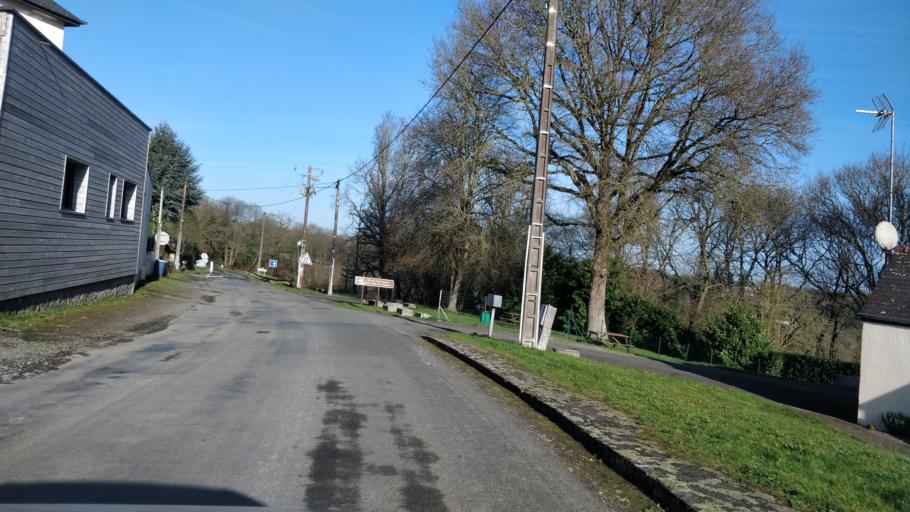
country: FR
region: Brittany
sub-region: Departement d'Ille-et-Vilaine
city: Sens-de-Bretagne
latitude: 48.3440
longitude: -1.4883
